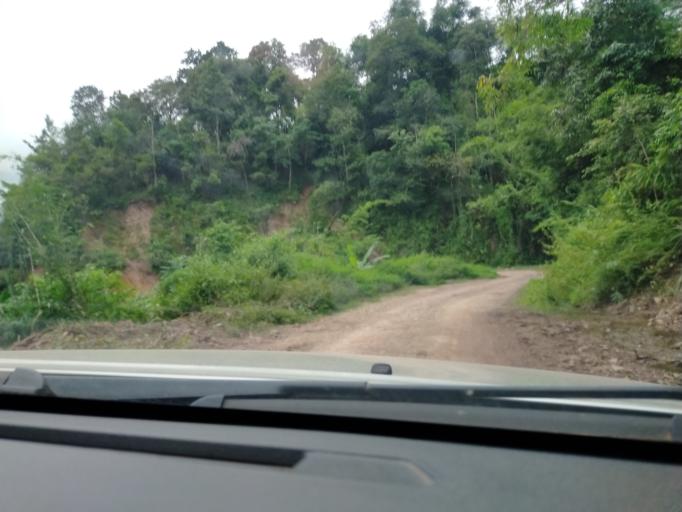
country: TH
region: Nan
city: Chaloem Phra Kiat
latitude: 19.7997
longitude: 101.3635
